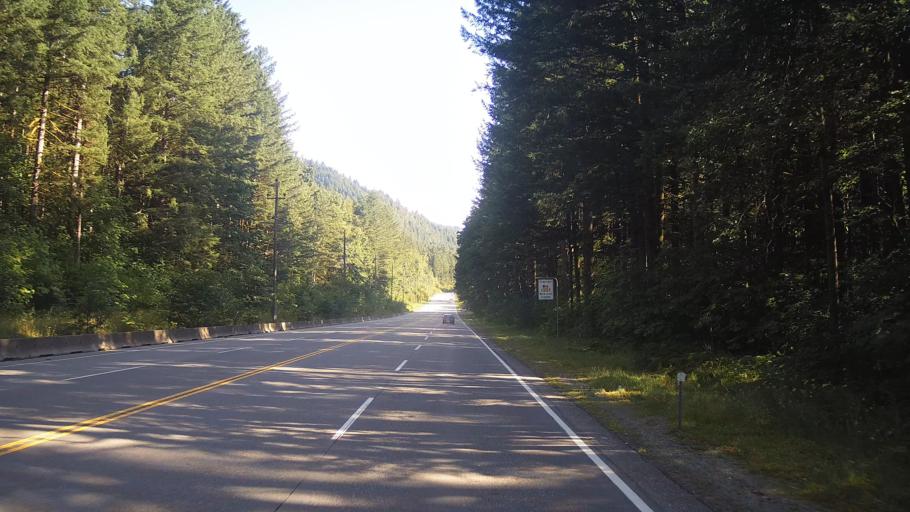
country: CA
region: British Columbia
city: Hope
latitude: 49.4544
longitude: -121.4365
